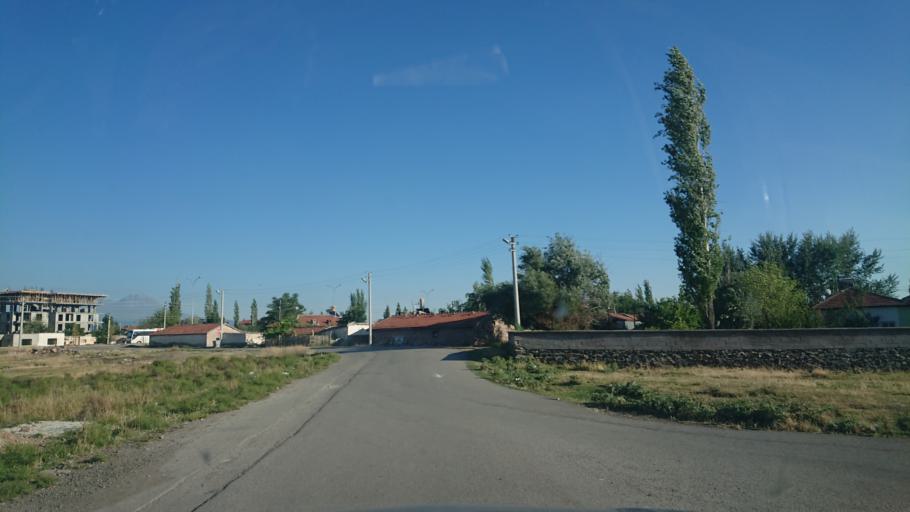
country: TR
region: Aksaray
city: Aksaray
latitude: 38.3830
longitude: 33.9912
